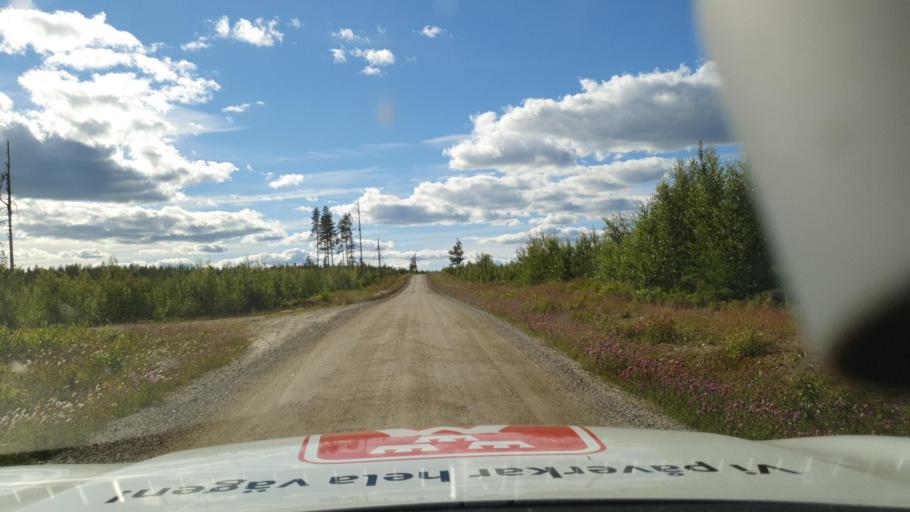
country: SE
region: Vaesterbotten
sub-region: Lycksele Kommun
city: Lycksele
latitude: 64.4009
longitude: 18.5685
